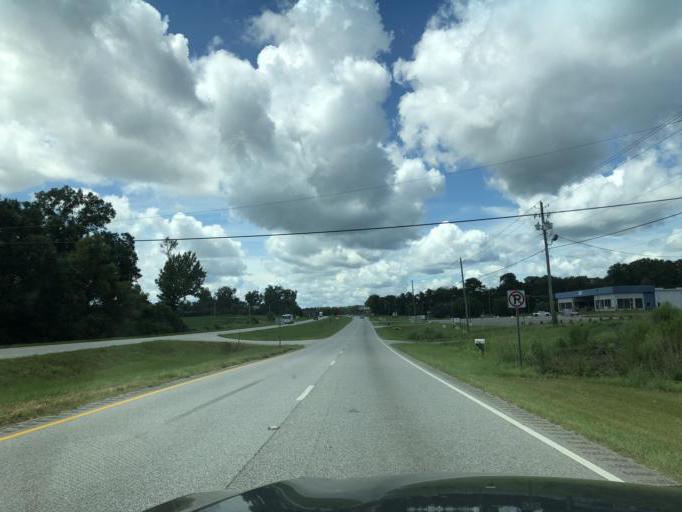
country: US
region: Alabama
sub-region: Barbour County
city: Eufaula
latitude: 31.9283
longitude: -85.1415
